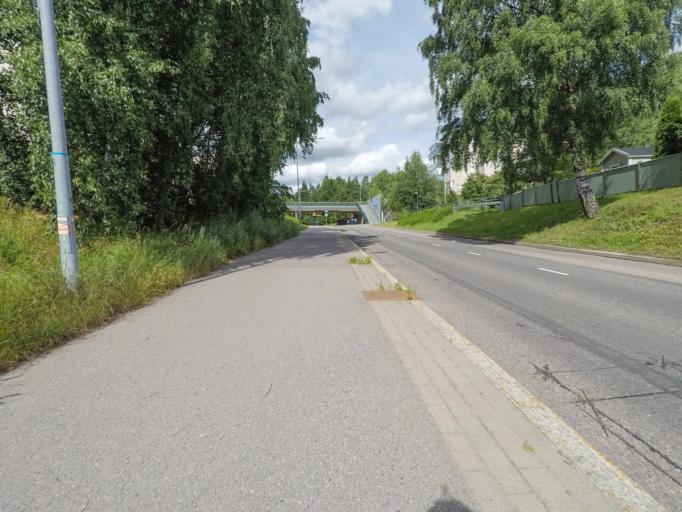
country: FI
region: Uusimaa
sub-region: Helsinki
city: Vantaa
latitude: 60.2294
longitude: 24.9994
